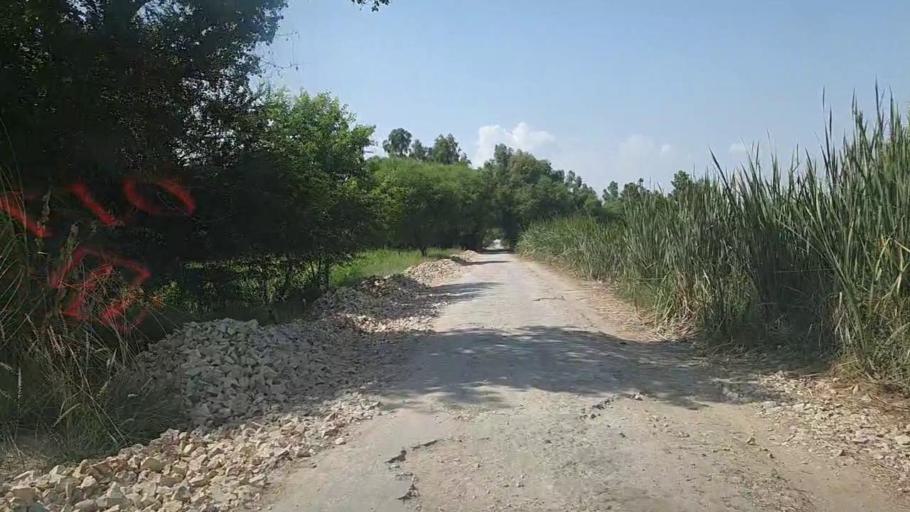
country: PK
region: Sindh
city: Khairpur
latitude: 28.0865
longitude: 69.6332
